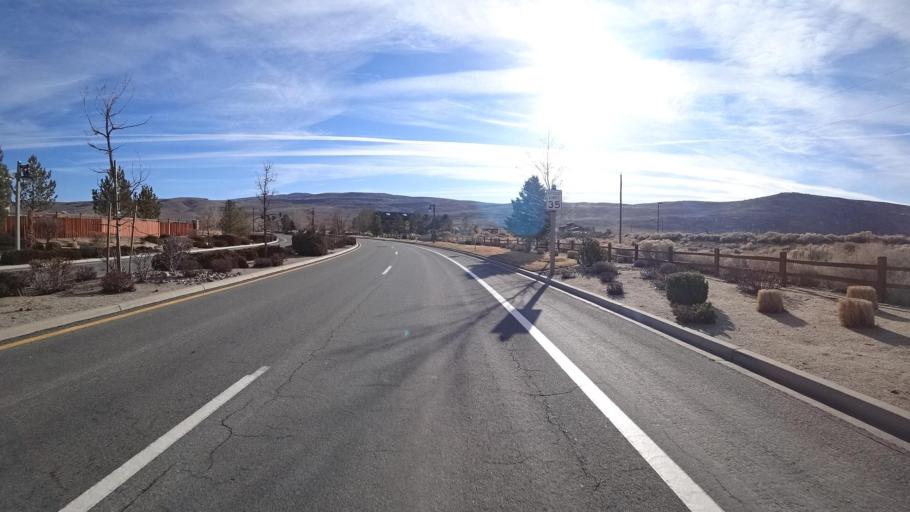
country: US
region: Nevada
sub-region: Washoe County
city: Spanish Springs
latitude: 39.6085
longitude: -119.6731
